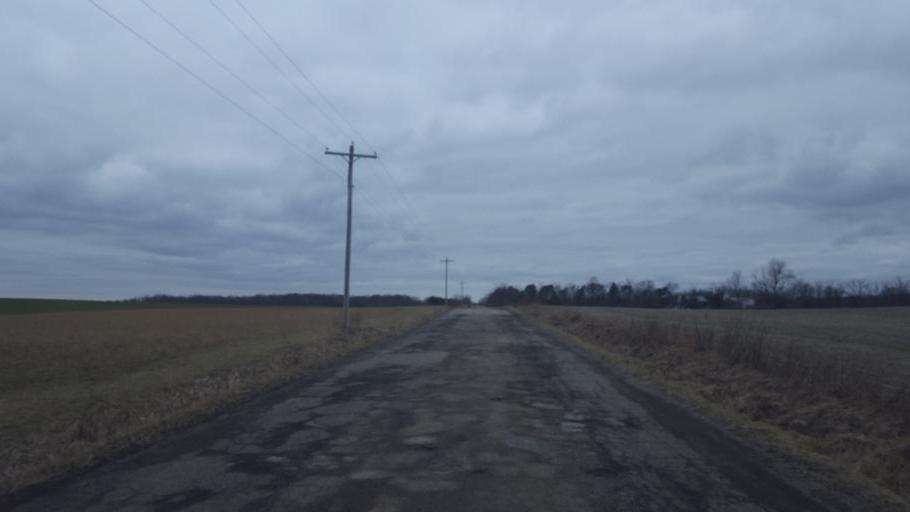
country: US
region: Ohio
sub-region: Morrow County
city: Mount Gilead
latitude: 40.5736
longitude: -82.7636
